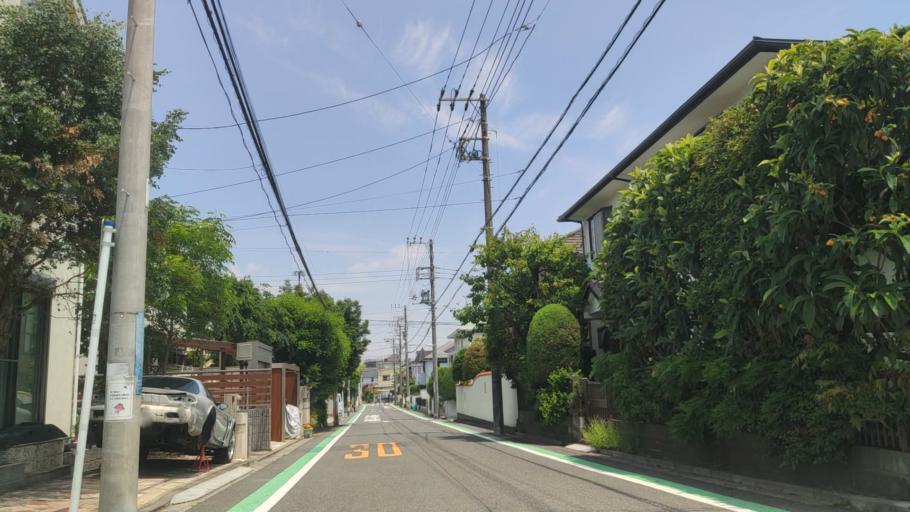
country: JP
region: Kanagawa
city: Yokohama
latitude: 35.4171
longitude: 139.6643
